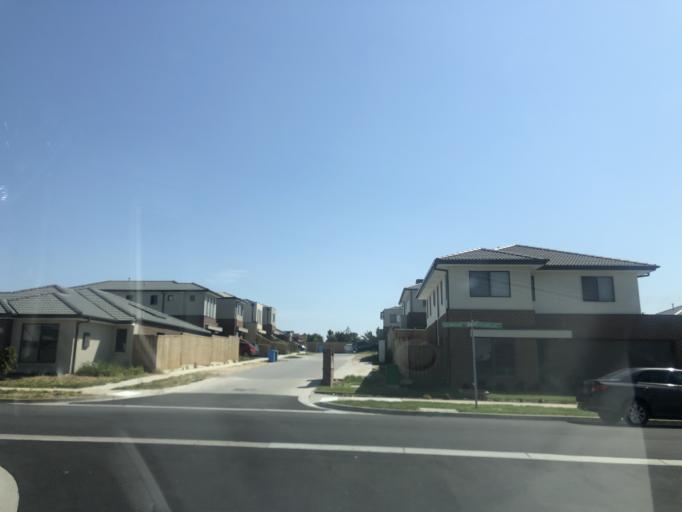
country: AU
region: Victoria
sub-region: Casey
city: Narre Warren South
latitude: -38.0482
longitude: 145.2763
